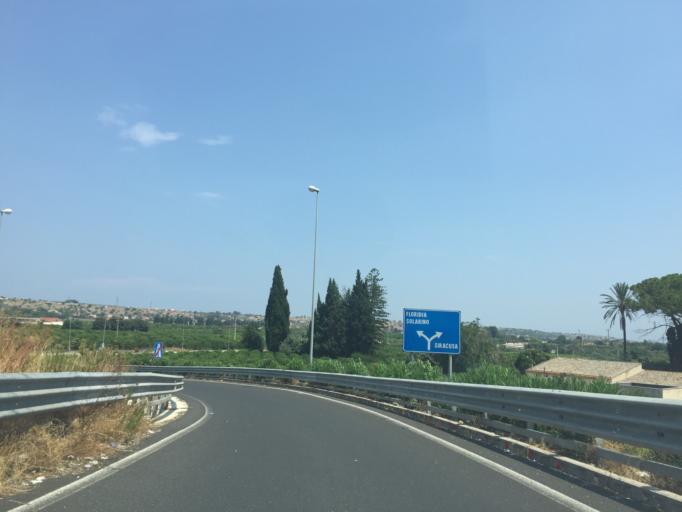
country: IT
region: Sicily
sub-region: Provincia di Siracusa
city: Belvedere
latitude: 37.0704
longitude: 15.2261
